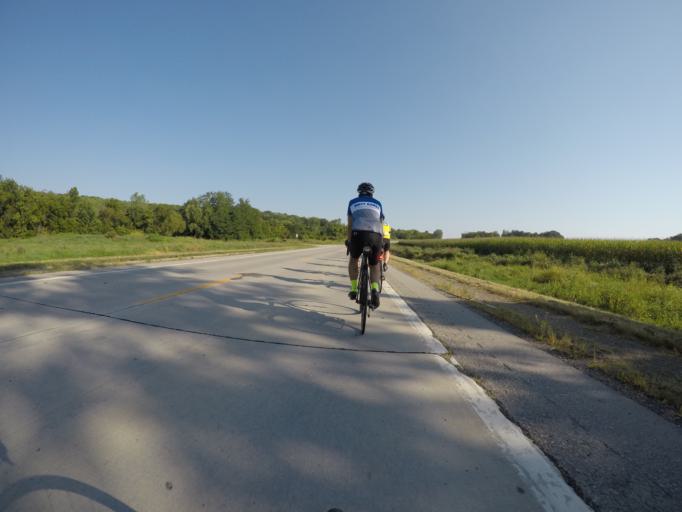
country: US
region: Missouri
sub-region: Platte County
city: Weston
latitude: 39.3826
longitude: -94.8649
